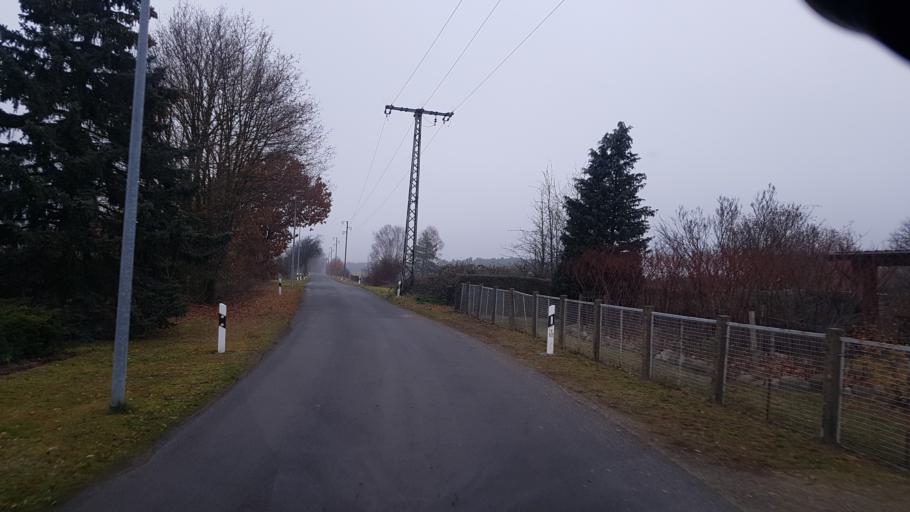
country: DE
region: Brandenburg
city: Altdobern
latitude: 51.6769
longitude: 13.9858
